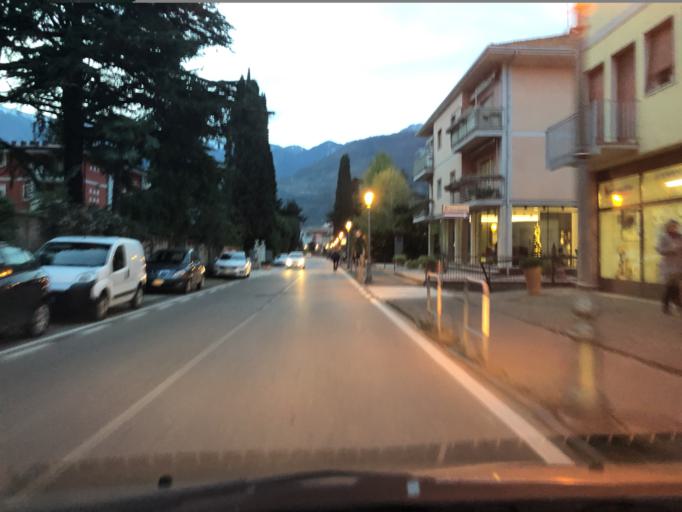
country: IT
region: Trentino-Alto Adige
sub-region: Provincia di Trento
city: Arco
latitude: 45.9189
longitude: 10.8824
